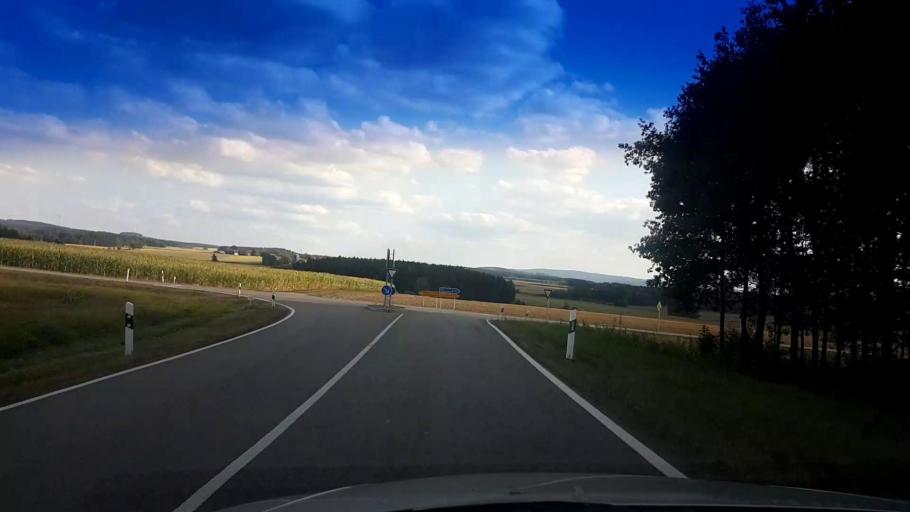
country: DE
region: Bavaria
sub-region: Upper Palatinate
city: Tirschenreuth
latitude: 49.8876
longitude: 12.3679
